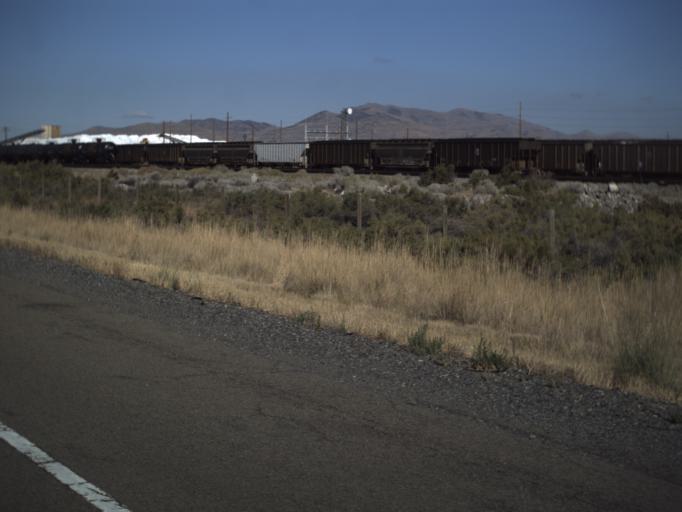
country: US
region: Utah
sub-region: Tooele County
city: Grantsville
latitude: 40.7456
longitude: -112.6474
